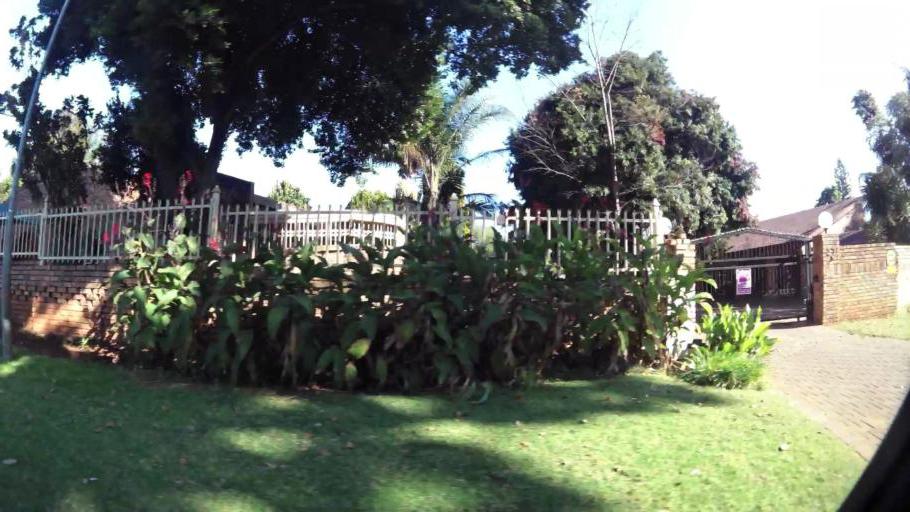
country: ZA
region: Gauteng
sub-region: City of Tshwane Metropolitan Municipality
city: Pretoria
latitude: -25.6679
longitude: 28.1457
